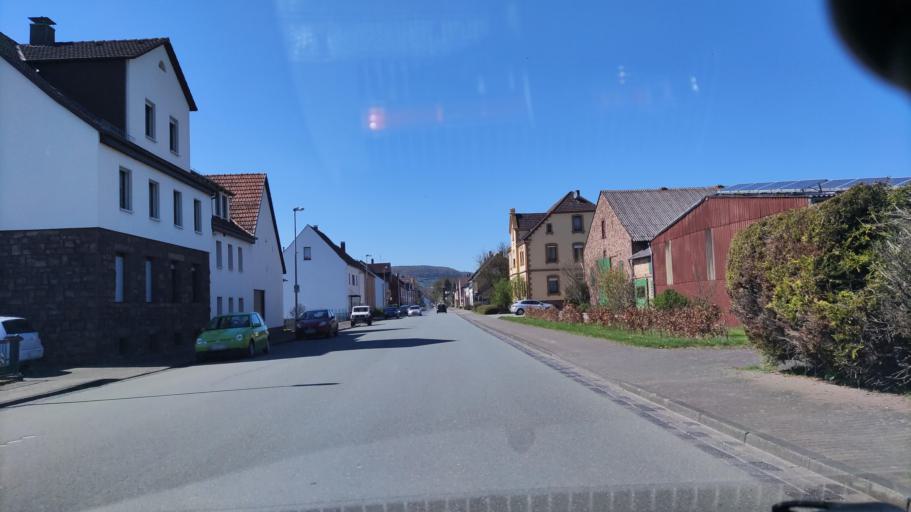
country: DE
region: North Rhine-Westphalia
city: Beverungen
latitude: 51.6603
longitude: 9.3908
